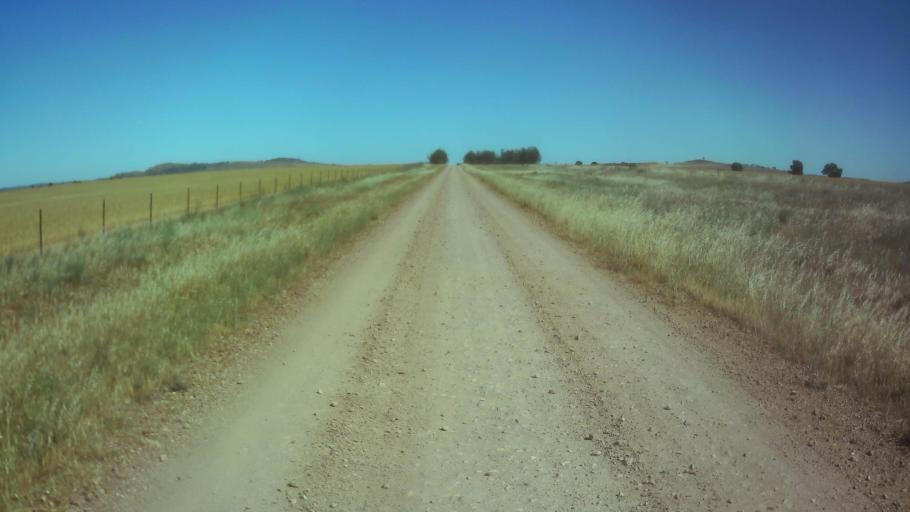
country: AU
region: New South Wales
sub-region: Weddin
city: Grenfell
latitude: -33.9866
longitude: 148.3346
